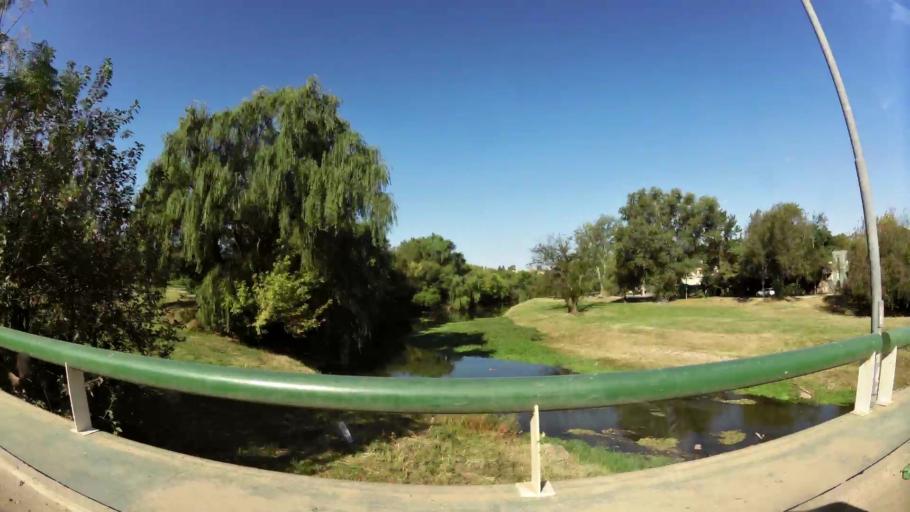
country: AR
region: Cordoba
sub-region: Departamento de Capital
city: Cordoba
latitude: -31.3749
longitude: -64.2487
